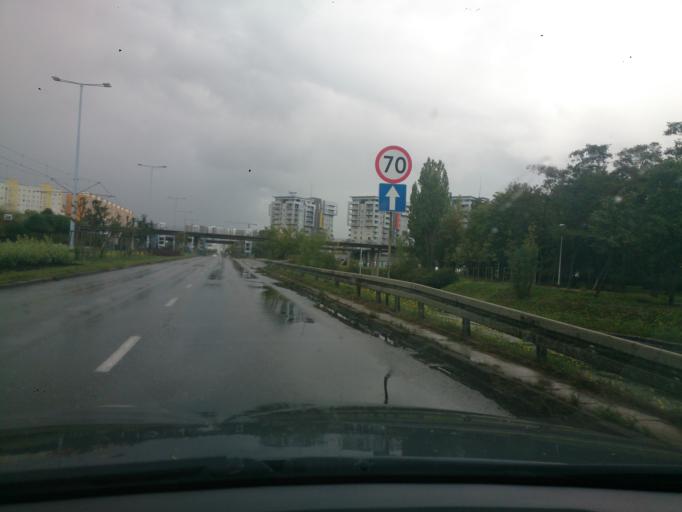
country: PL
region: Pomeranian Voivodeship
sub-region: Gdansk
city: Gdansk
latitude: 54.3935
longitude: 18.6037
